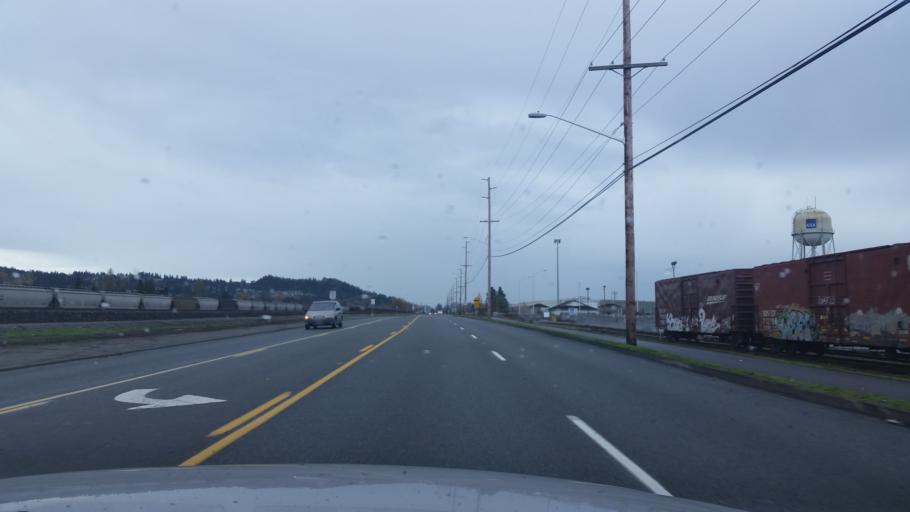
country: US
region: Washington
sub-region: King County
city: Auburn
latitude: 47.2867
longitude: -122.2317
